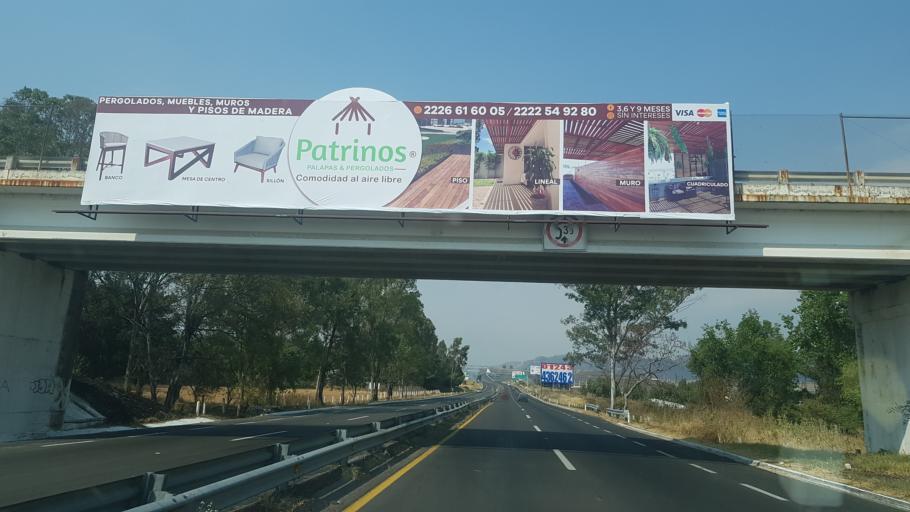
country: MX
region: Puebla
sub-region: Atlixco
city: San Agustin Huixaxtla
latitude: 18.9283
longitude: -98.3978
